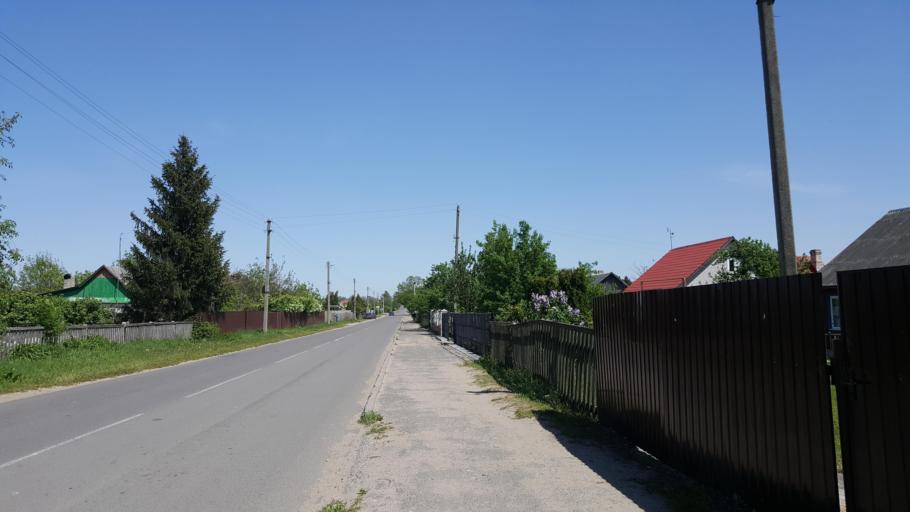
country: BY
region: Brest
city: Brest
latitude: 52.1580
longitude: 23.6462
